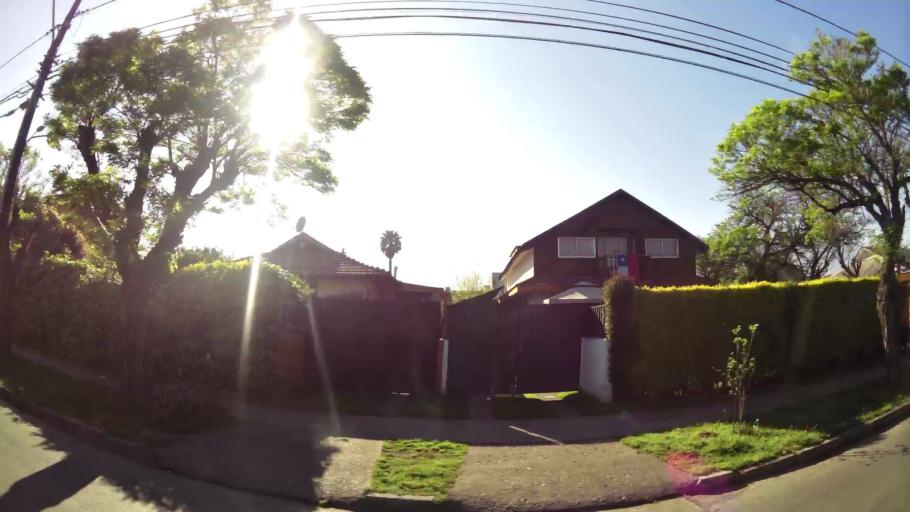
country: CL
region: Santiago Metropolitan
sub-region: Provincia de Santiago
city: Villa Presidente Frei, Nunoa, Santiago, Chile
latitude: -33.4579
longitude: -70.5595
